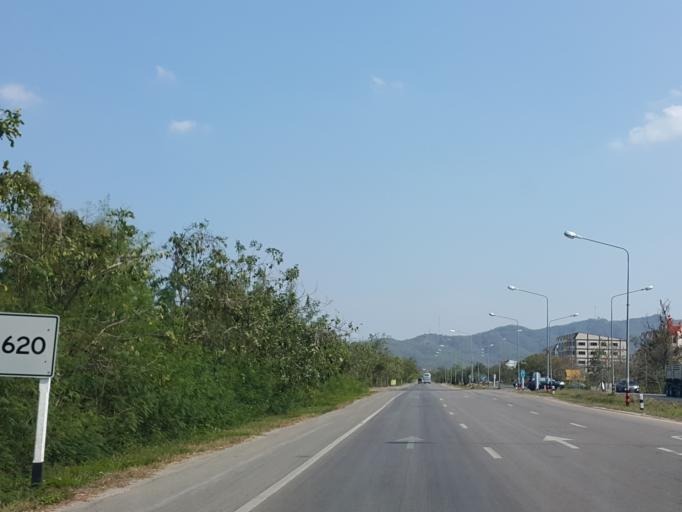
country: TH
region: Lampang
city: Lampang
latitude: 18.2725
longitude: 99.5241
